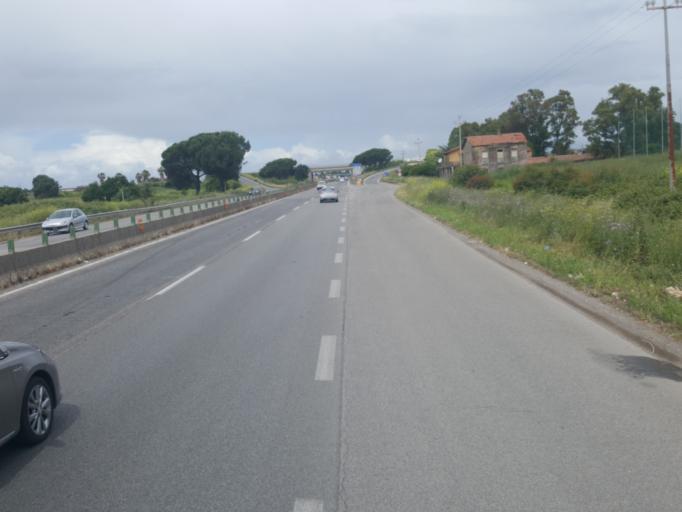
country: IT
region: Latium
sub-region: Provincia di Latina
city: Aprilia
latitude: 41.5703
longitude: 12.6671
